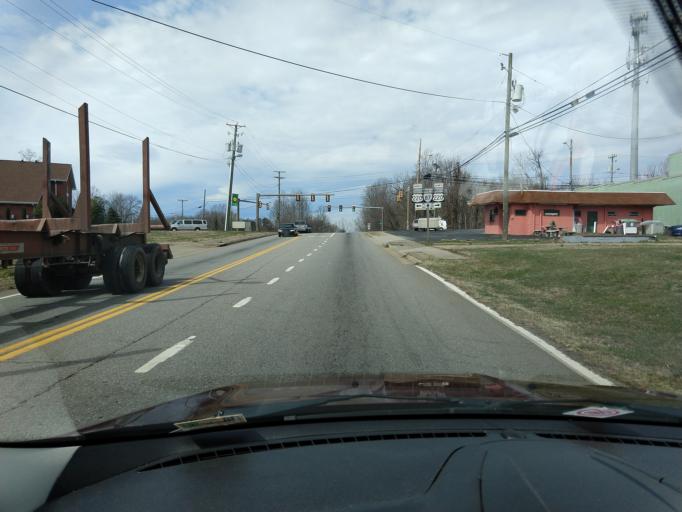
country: US
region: Virginia
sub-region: Henry County
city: Chatmoss
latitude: 36.5766
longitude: -79.8577
